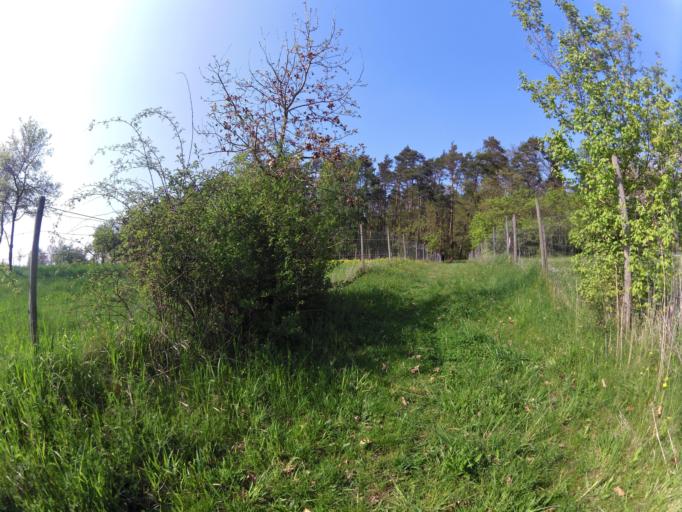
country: DE
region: Bavaria
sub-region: Regierungsbezirk Unterfranken
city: Sommerhausen
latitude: 49.7013
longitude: 10.0424
